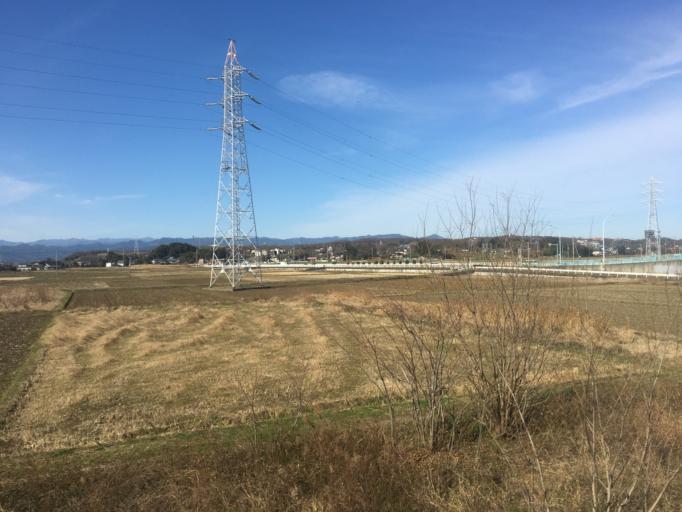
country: JP
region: Saitama
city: Sakado
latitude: 35.9900
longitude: 139.4006
